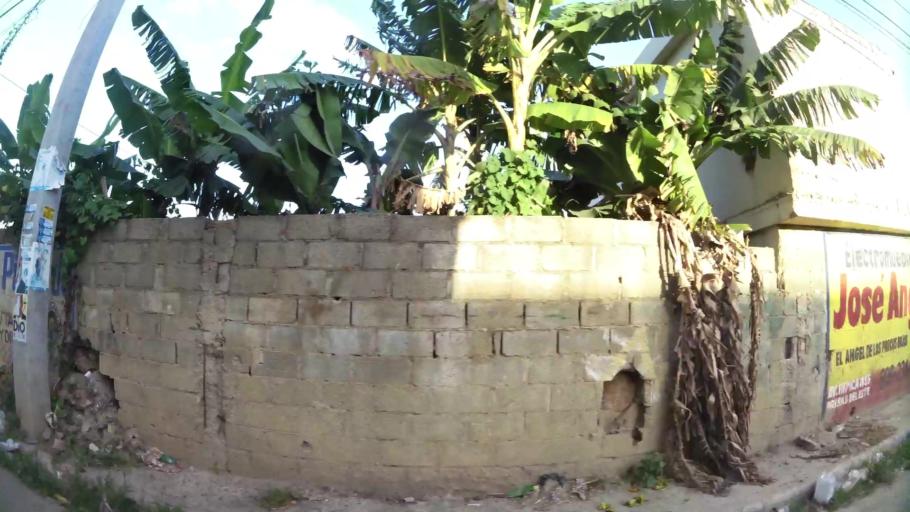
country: DO
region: Santo Domingo
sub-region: Santo Domingo
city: Santo Domingo Este
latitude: 18.4803
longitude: -69.8286
